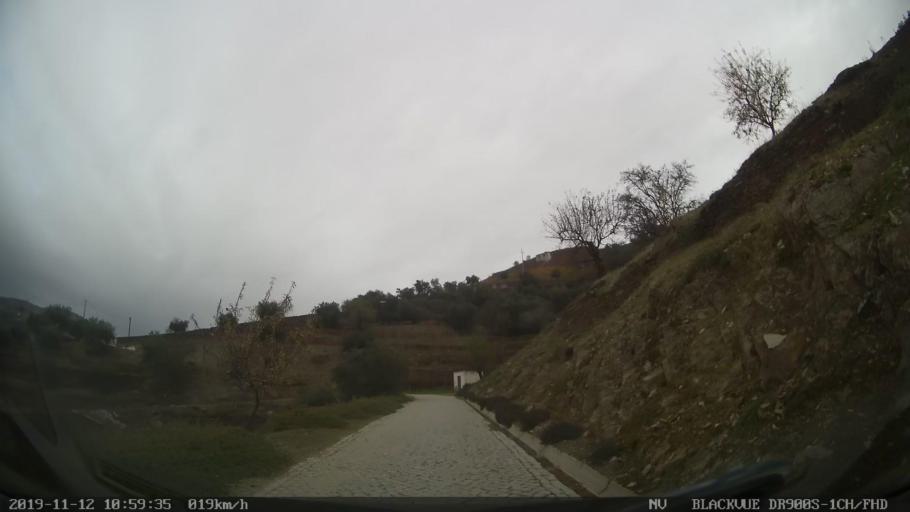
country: PT
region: Vila Real
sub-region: Sabrosa
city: Vilela
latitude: 41.2093
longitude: -7.5348
